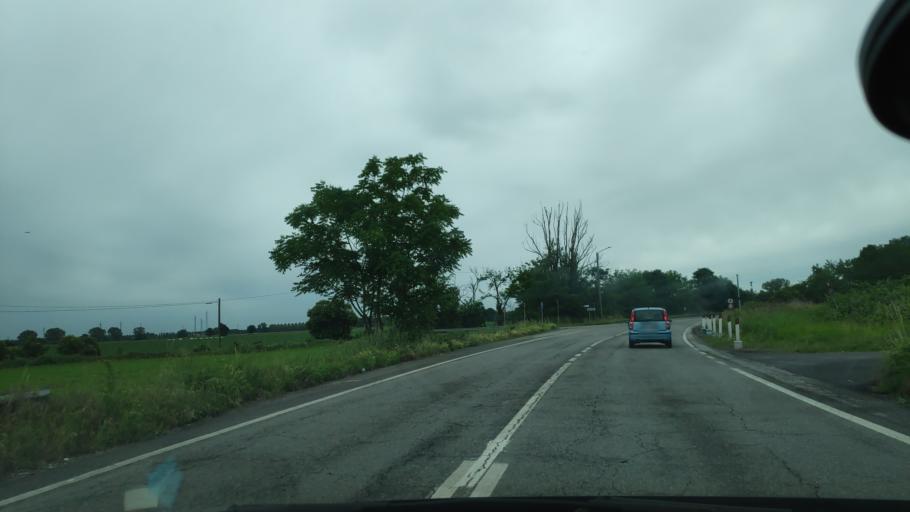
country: IT
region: Lombardy
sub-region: Citta metropolitana di Milano
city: Civesio
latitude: 45.3799
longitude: 9.2620
